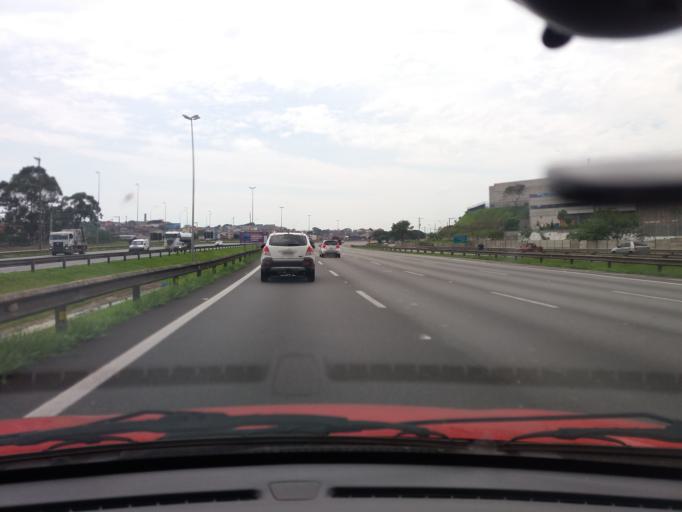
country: BR
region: Sao Paulo
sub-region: Carapicuiba
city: Carapicuiba
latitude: -23.5521
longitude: -46.8199
